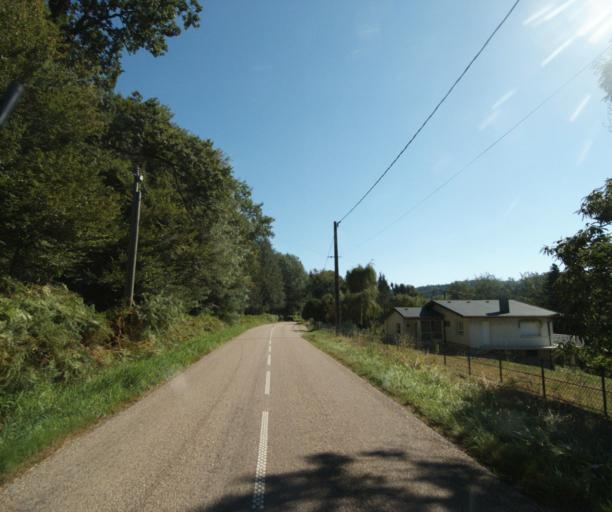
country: FR
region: Lorraine
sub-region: Departement des Vosges
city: Arches
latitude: 48.1464
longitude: 6.4924
